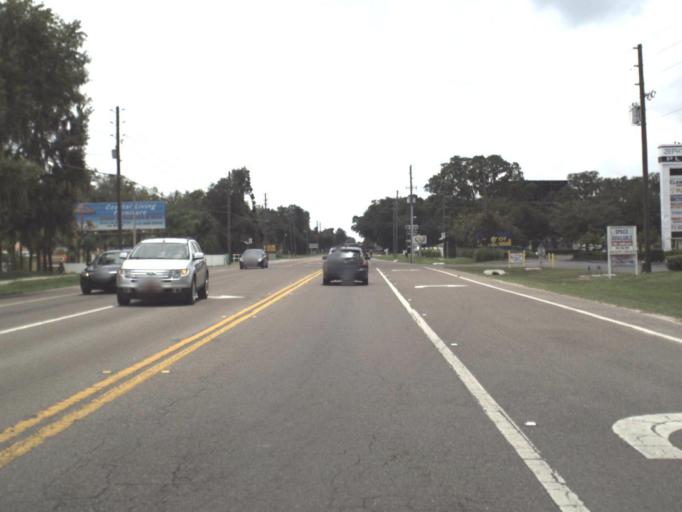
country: US
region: Florida
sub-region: Pasco County
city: Zephyrhills West
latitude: 28.2299
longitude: -82.2131
